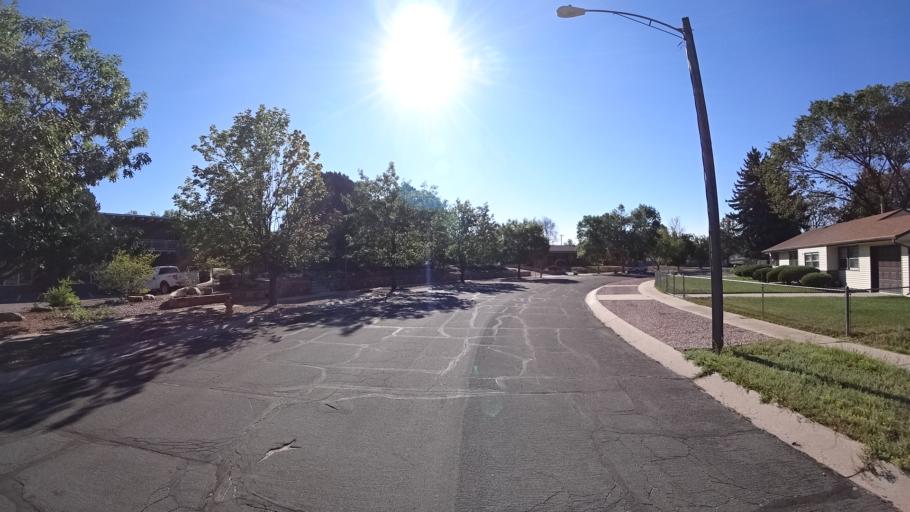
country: US
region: Colorado
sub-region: El Paso County
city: Colorado Springs
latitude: 38.8687
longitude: -104.7978
